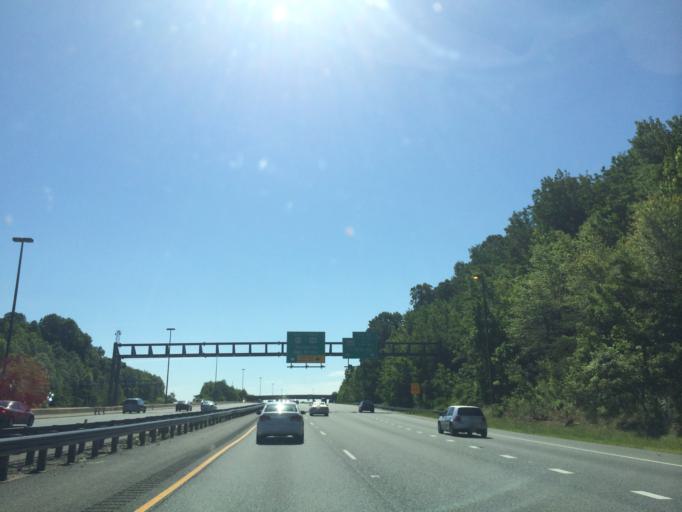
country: US
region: Maryland
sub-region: Anne Arundel County
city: Edgewater
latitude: 38.9835
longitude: -76.5664
